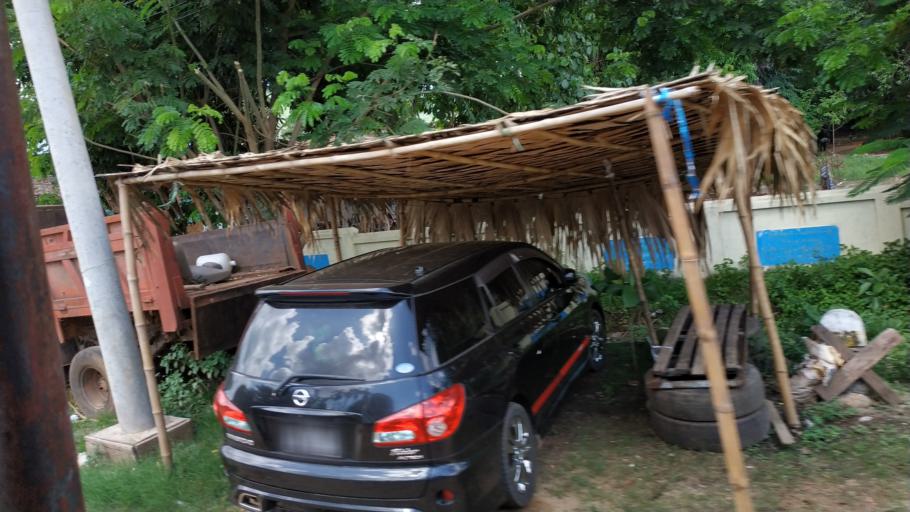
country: MM
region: Mon
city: Kyaikto
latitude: 17.4025
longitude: 97.0765
